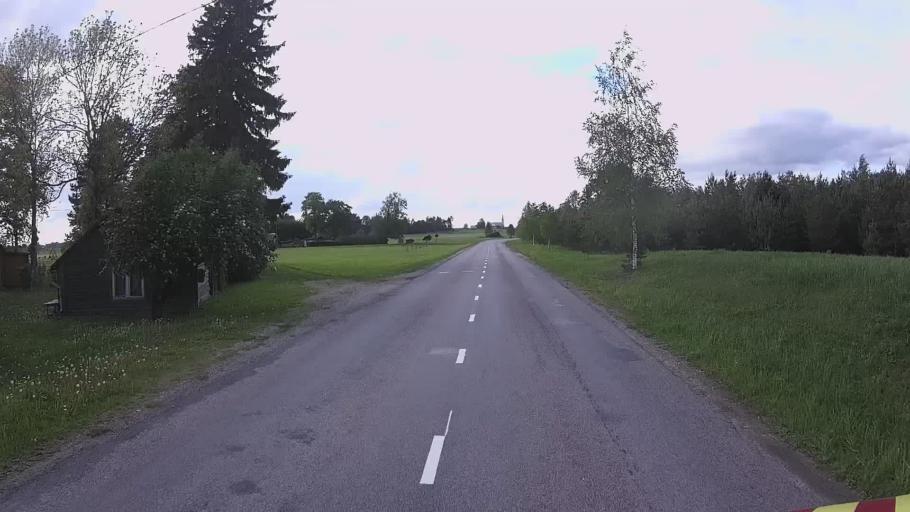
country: EE
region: Jogevamaa
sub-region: Mustvee linn
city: Mustvee
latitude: 59.0275
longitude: 27.0819
